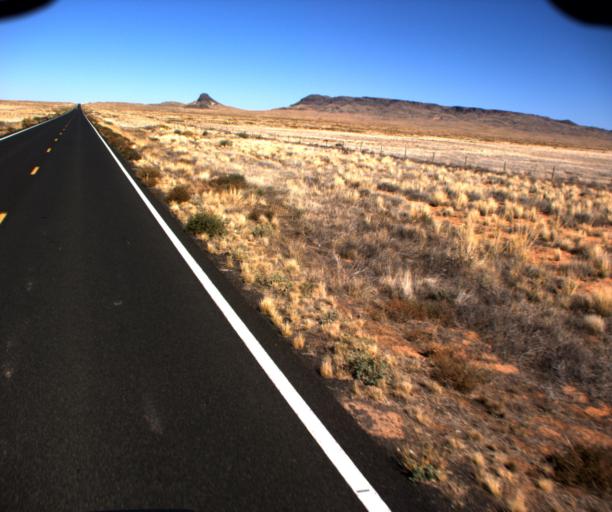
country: US
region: Arizona
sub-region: Navajo County
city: Dilkon
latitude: 35.3756
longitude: -110.4252
